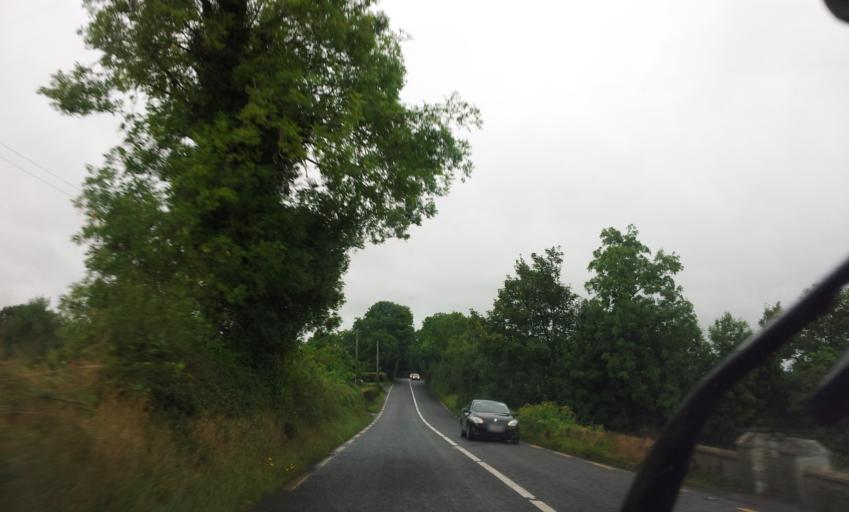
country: IE
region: Munster
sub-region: County Cork
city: Mitchelstown
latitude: 52.2599
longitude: -8.3297
